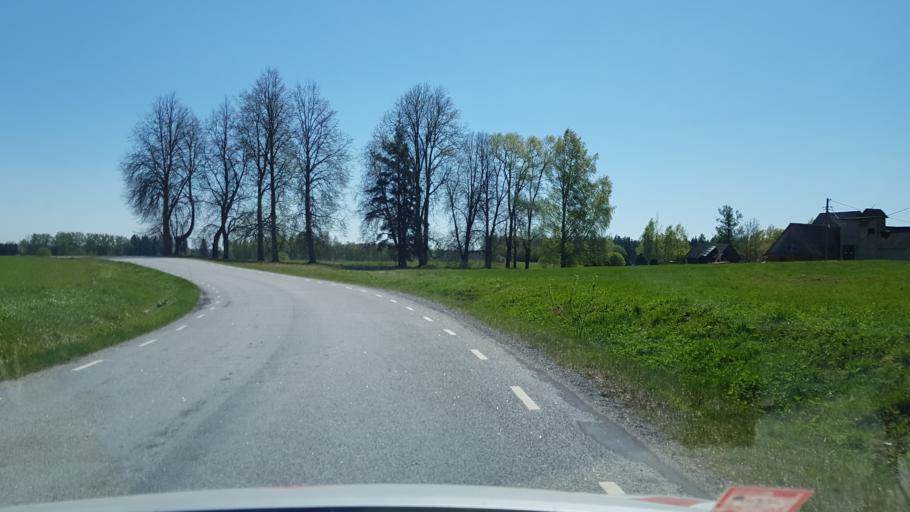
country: EE
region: Vorumaa
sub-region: Voru linn
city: Voru
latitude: 57.9115
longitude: 26.9581
